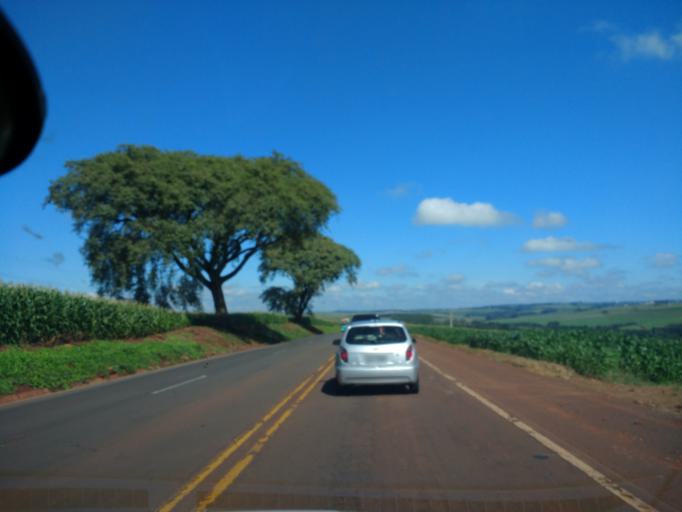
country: BR
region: Parana
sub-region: Cianorte
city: Cianorte
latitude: -23.6451
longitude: -52.4837
